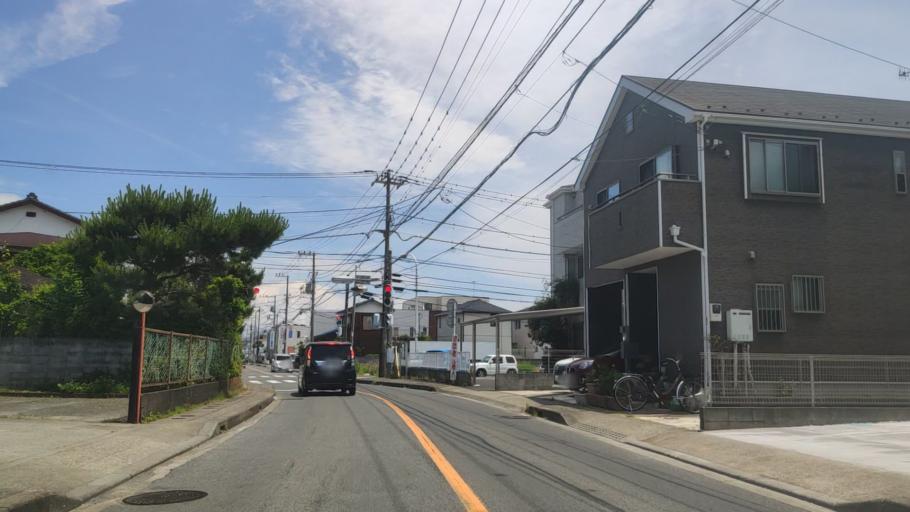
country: JP
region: Kanagawa
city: Chigasaki
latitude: 35.3384
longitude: 139.3824
